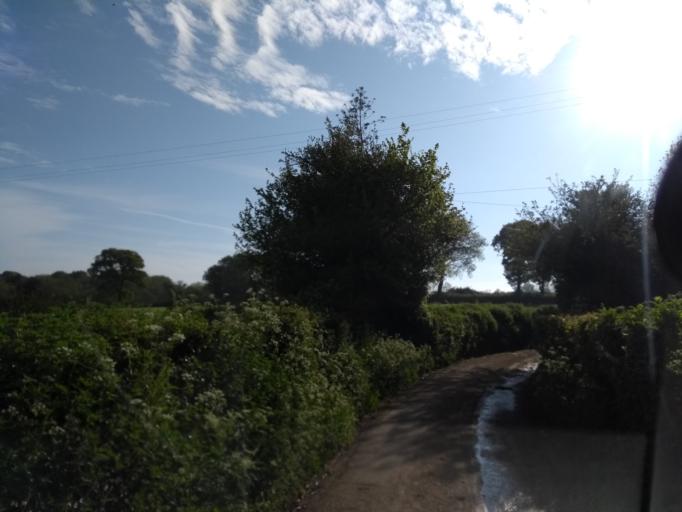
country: GB
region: England
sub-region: Dorset
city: Lyme Regis
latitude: 50.7982
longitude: -2.9079
